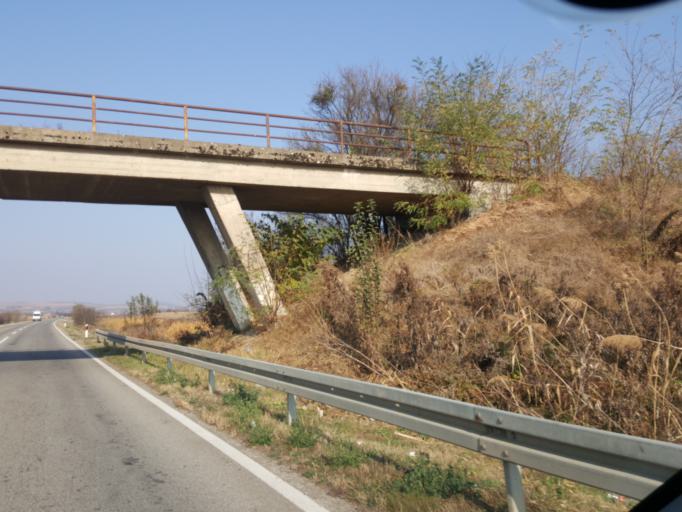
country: RS
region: Central Serbia
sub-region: Jablanicki Okrug
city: Leskovac
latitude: 43.0334
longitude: 21.9416
